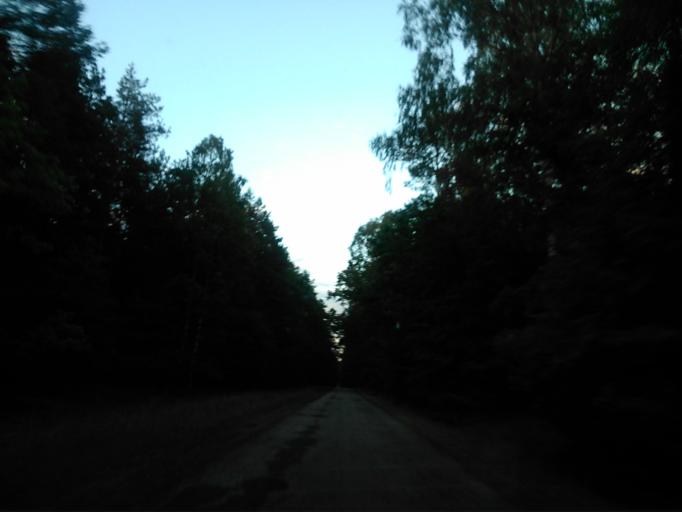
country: PL
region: Kujawsko-Pomorskie
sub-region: Powiat golubsko-dobrzynski
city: Radomin
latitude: 53.1559
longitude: 19.1499
